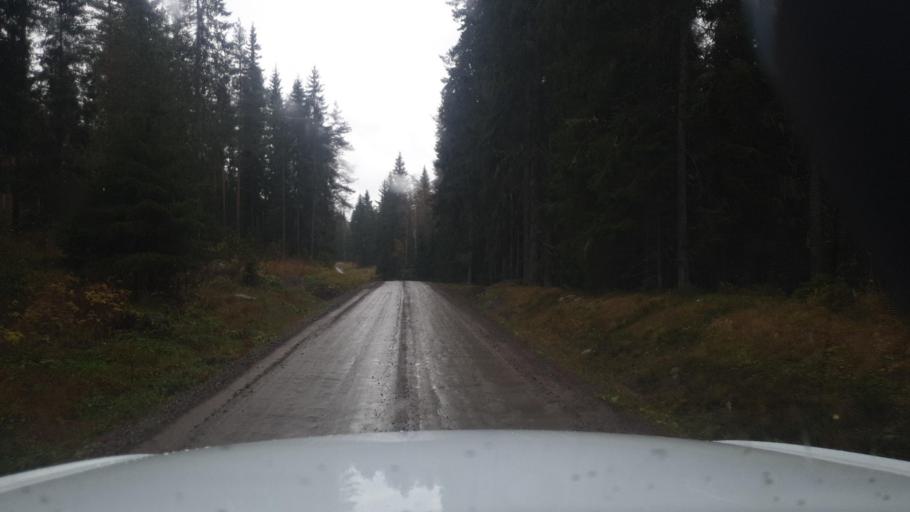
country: SE
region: Vaermland
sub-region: Eda Kommun
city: Charlottenberg
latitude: 60.0368
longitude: 12.5909
